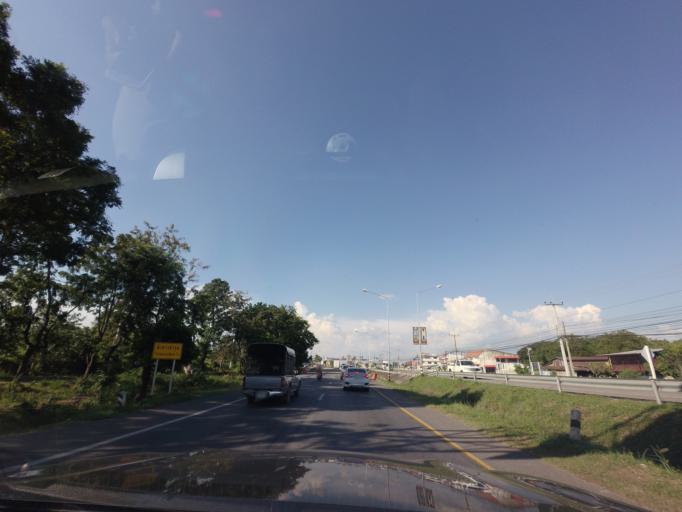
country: TH
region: Khon Kaen
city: Non Sila
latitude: 15.9645
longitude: 102.6908
